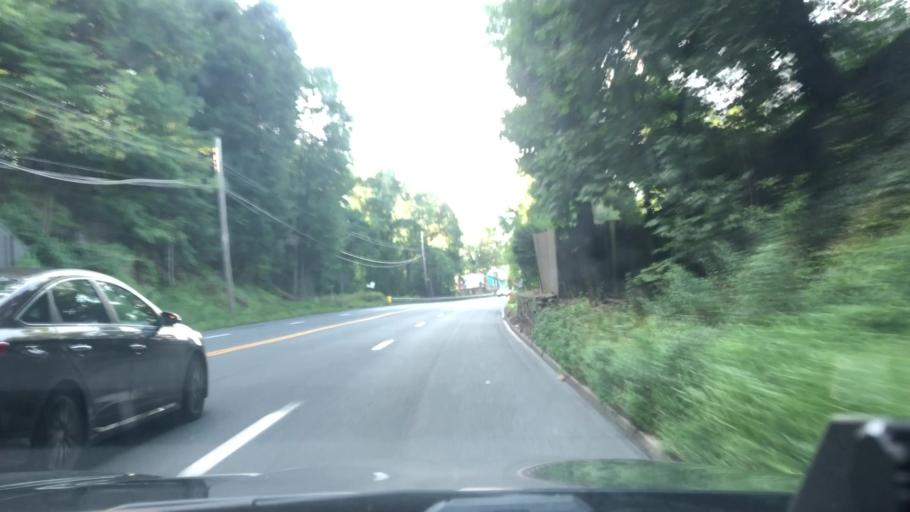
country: US
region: Pennsylvania
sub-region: Lehigh County
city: Fountain Hill
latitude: 40.5960
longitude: -75.3899
